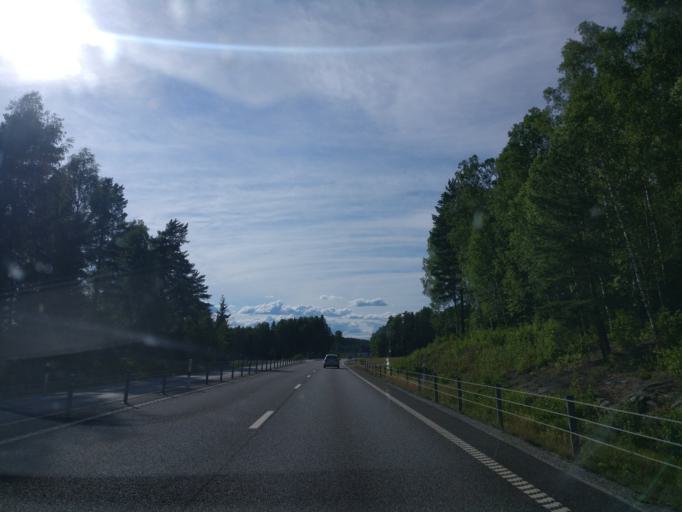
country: SE
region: Vaermland
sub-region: Arvika Kommun
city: Arvika
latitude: 59.6541
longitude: 12.6575
